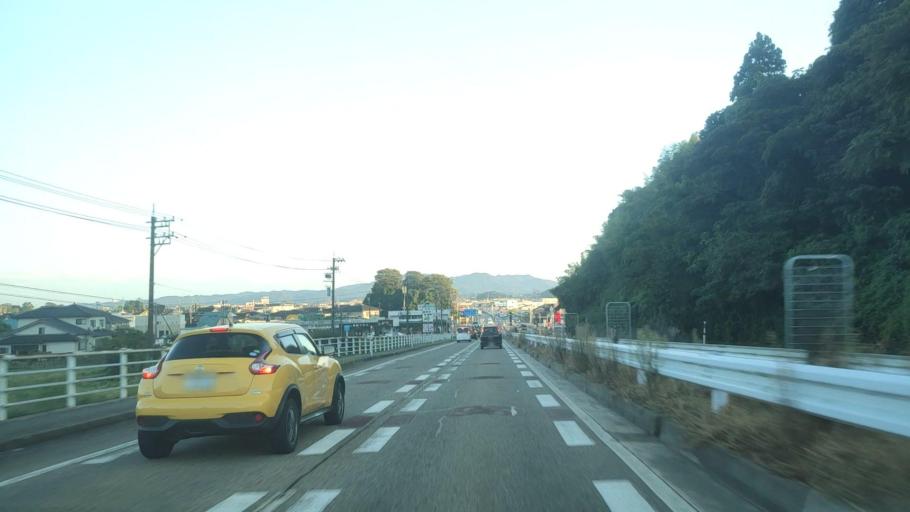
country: JP
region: Toyama
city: Himi
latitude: 36.8476
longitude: 136.9802
